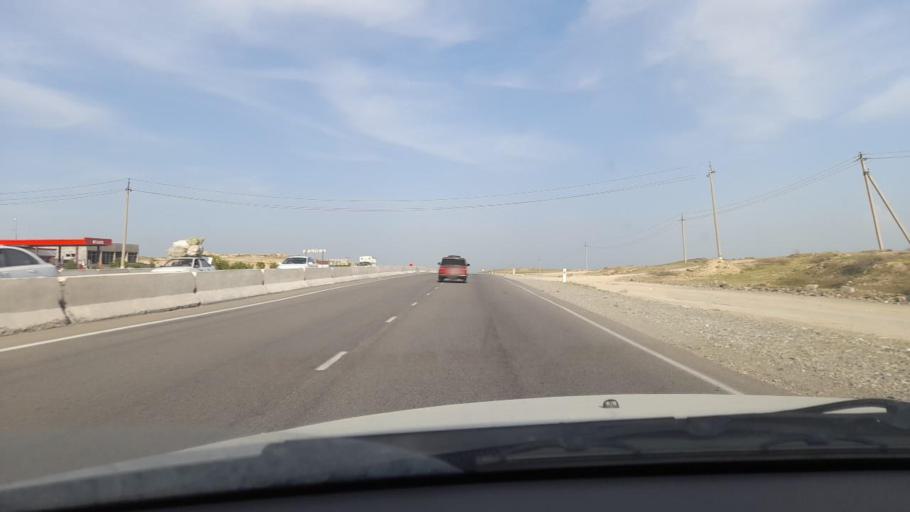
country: UZ
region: Jizzax
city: Jizzax
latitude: 40.0553
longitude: 67.8099
